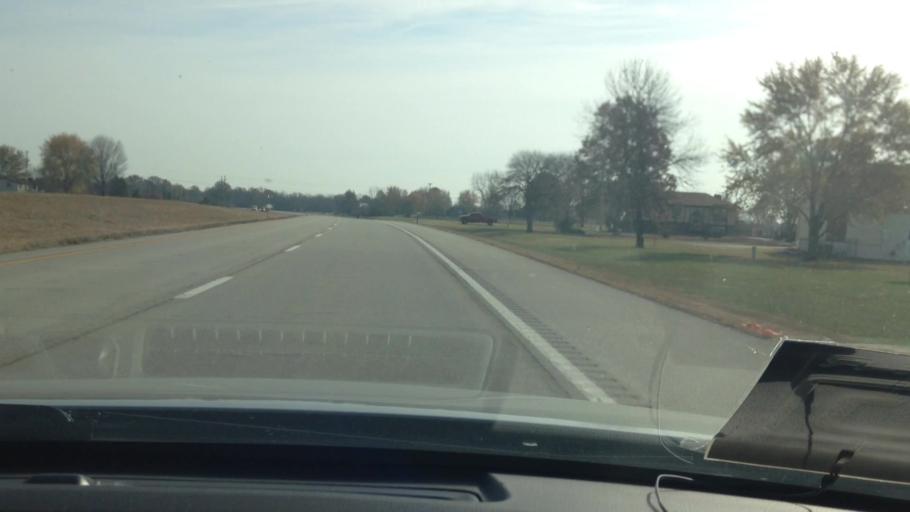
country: US
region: Missouri
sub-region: Cass County
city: Harrisonville
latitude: 38.6131
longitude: -94.3265
